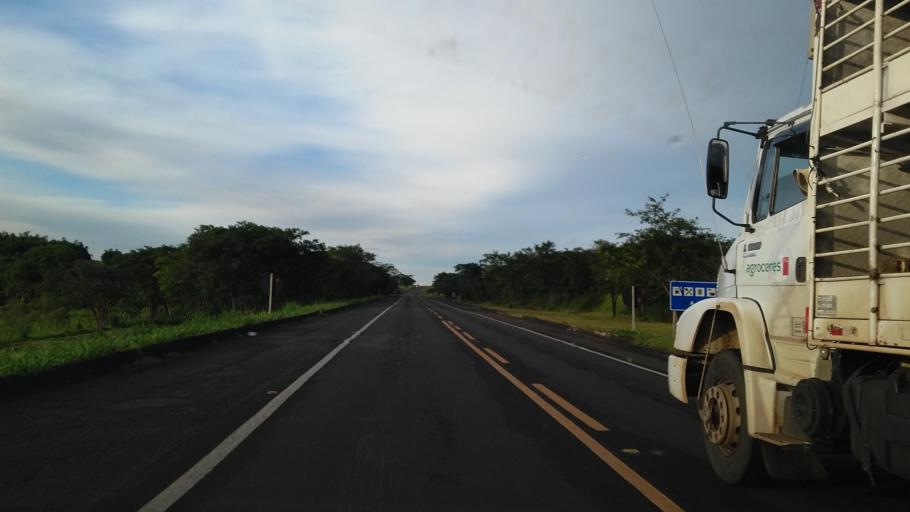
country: BR
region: Sao Paulo
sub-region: Marilia
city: Marilia
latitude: -21.9252
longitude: -49.9175
